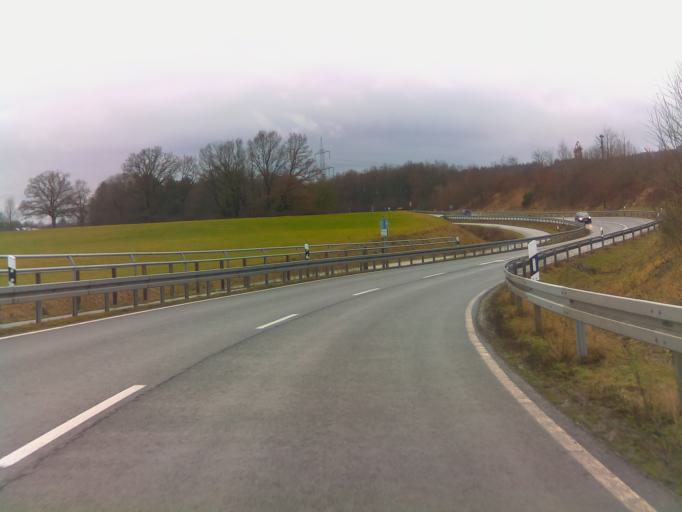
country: DE
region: Hesse
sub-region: Regierungsbezirk Kassel
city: Flieden
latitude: 50.3940
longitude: 9.5410
